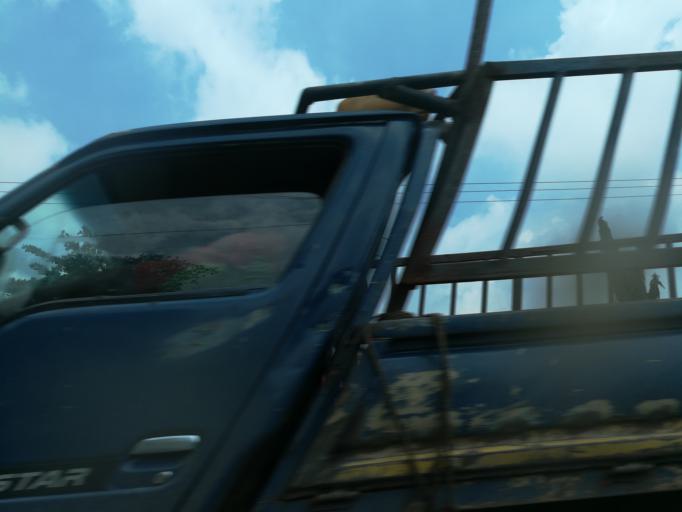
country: NG
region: Lagos
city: Ikorodu
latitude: 6.6716
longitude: 3.5124
